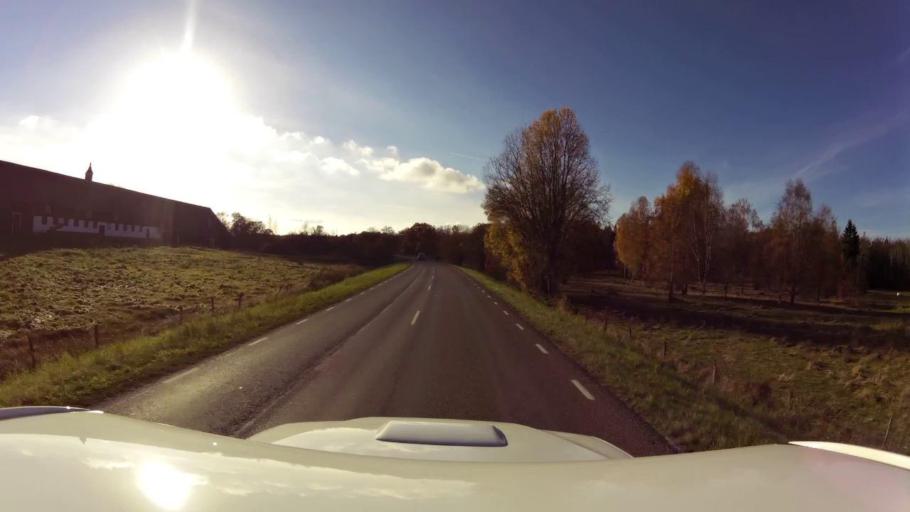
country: SE
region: OEstergoetland
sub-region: Linkopings Kommun
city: Malmslatt
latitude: 58.3462
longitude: 15.5253
